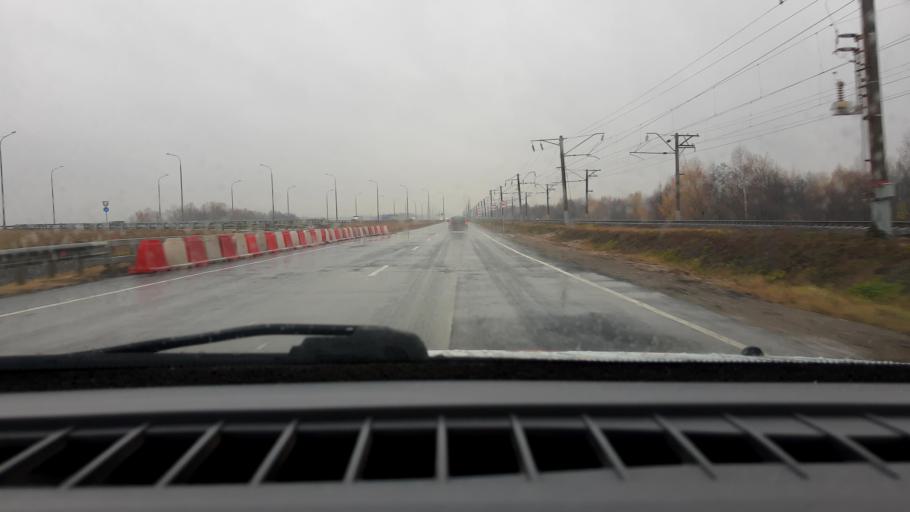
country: RU
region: Nizjnij Novgorod
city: Neklyudovo
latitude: 56.3926
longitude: 43.9773
